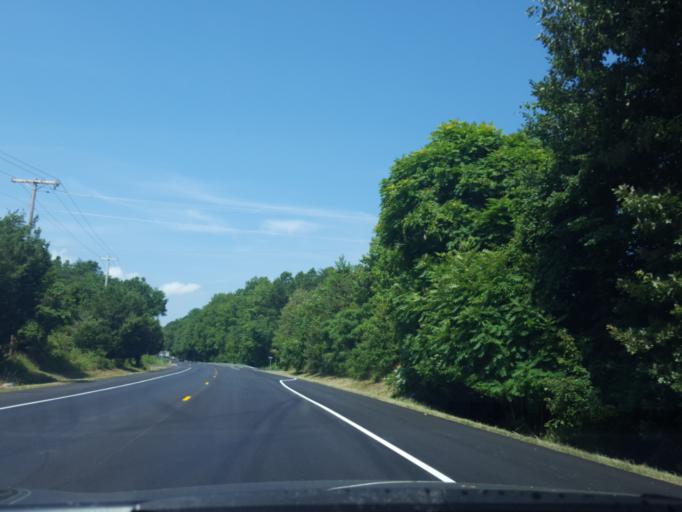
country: US
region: Maryland
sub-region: Saint Mary's County
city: Charlotte Hall
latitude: 38.4118
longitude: -76.8694
